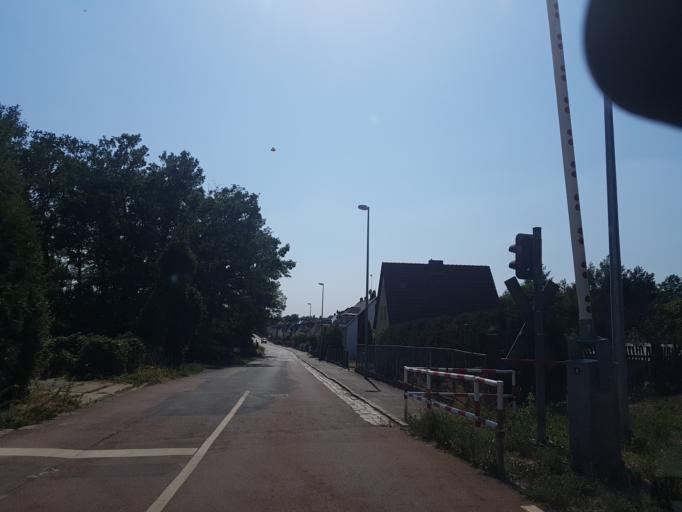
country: DE
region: Saxony-Anhalt
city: Coswig
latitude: 51.8859
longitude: 12.4675
